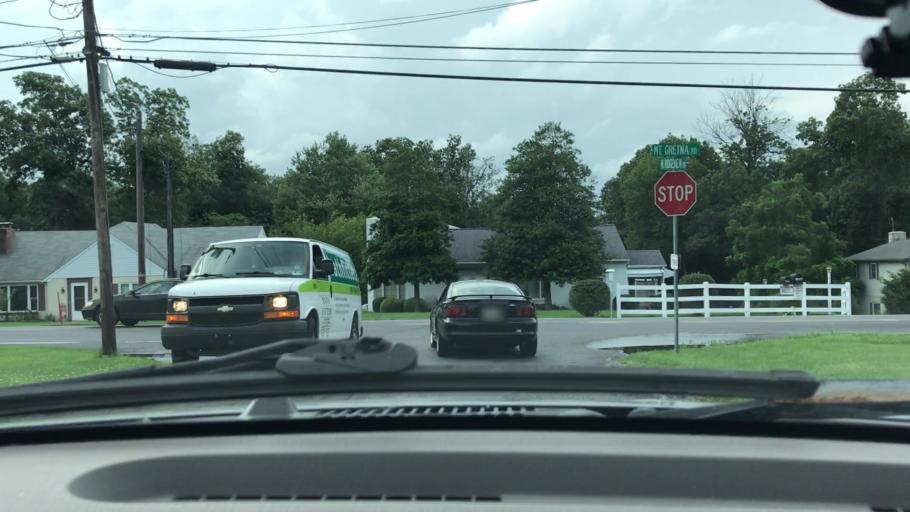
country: US
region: Pennsylvania
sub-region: Lancaster County
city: Elizabethtown
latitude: 40.1769
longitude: -76.5910
